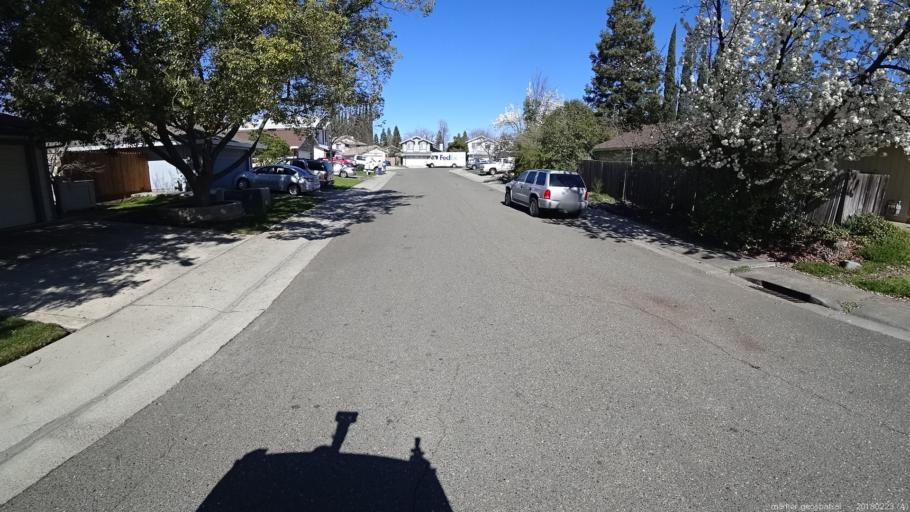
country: US
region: California
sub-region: Sacramento County
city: North Highlands
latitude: 38.7147
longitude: -121.3871
